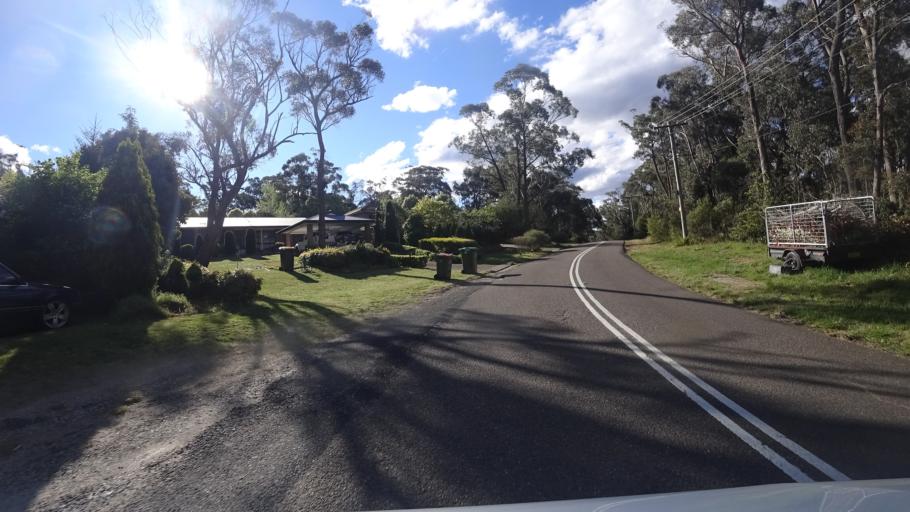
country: AU
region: New South Wales
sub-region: Blue Mountains Municipality
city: Katoomba
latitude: -33.7211
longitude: 150.2883
